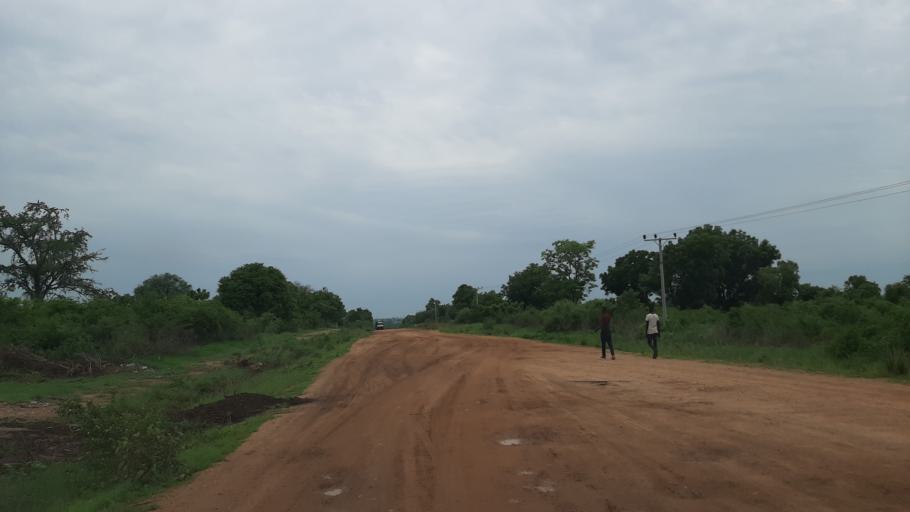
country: ET
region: Gambela
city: Gambela
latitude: 8.2297
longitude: 34.5699
